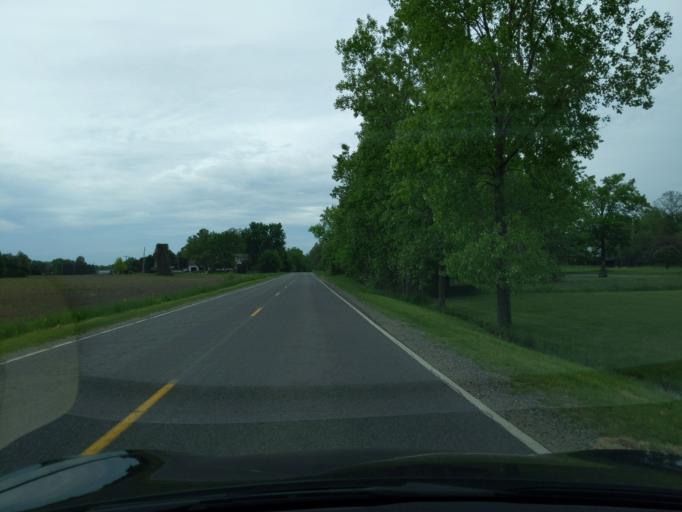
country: US
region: Michigan
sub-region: Ingham County
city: Leslie
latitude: 42.4612
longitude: -84.3513
